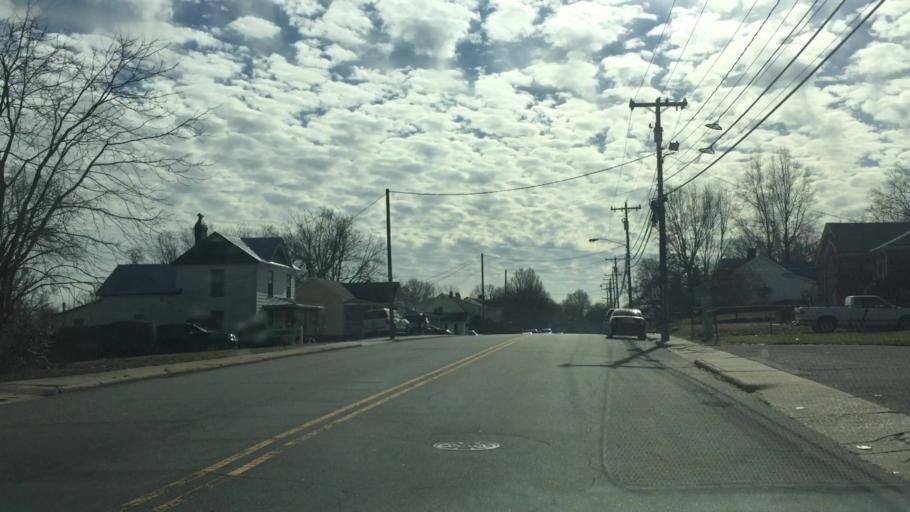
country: US
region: North Carolina
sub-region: Rockingham County
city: Reidsville
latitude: 36.3563
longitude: -79.6560
